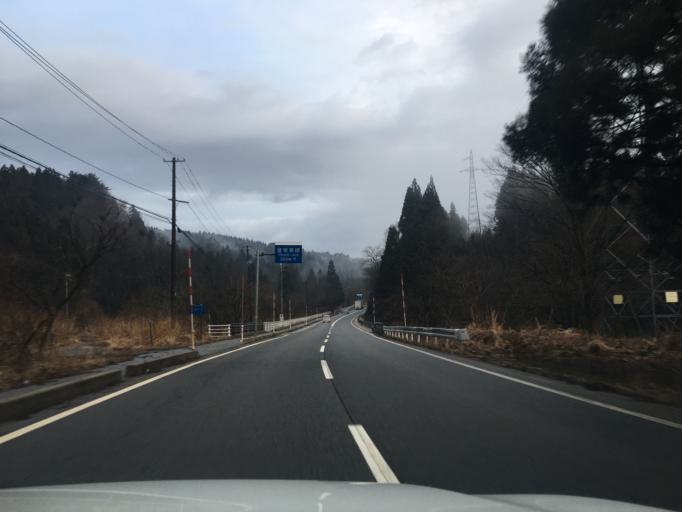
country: JP
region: Niigata
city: Murakami
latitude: 38.3684
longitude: 139.5530
